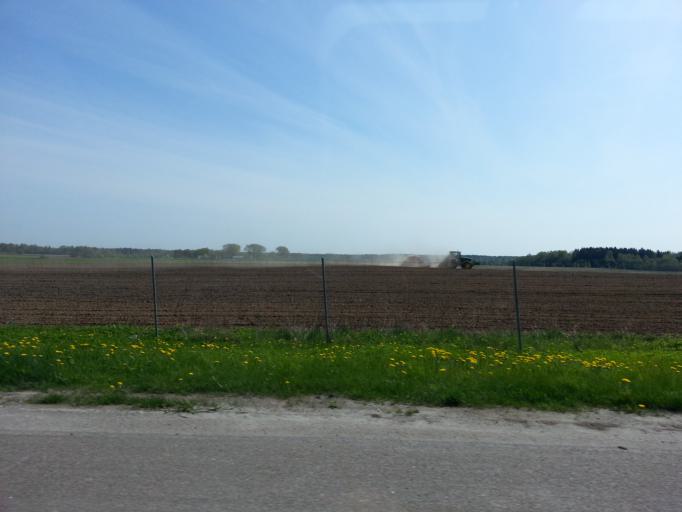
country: LT
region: Vilnius County
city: Ukmerge
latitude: 55.1384
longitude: 24.8318
